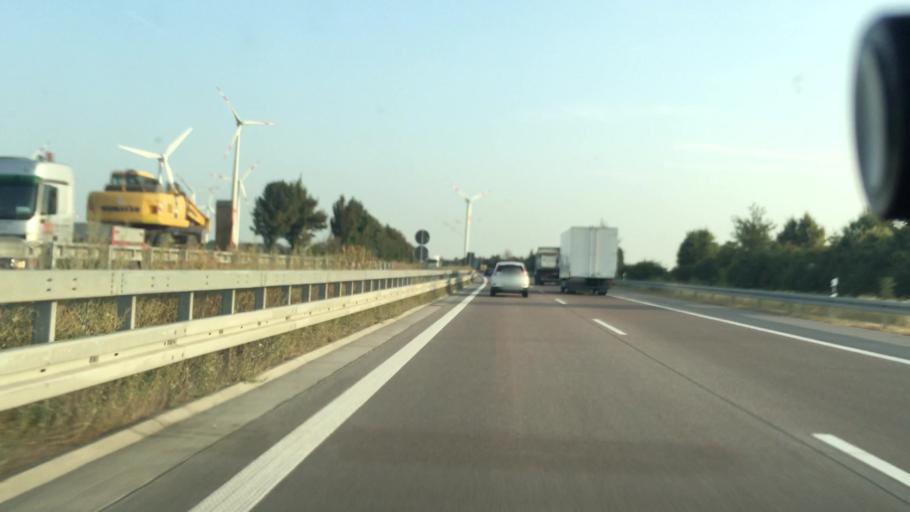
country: DE
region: Saxony-Anhalt
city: Nauendorf
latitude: 51.6123
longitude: 11.8704
